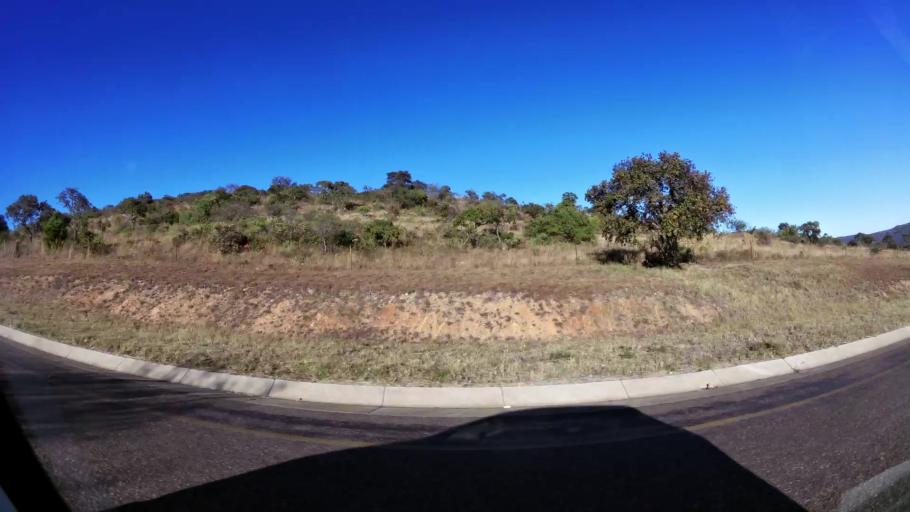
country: ZA
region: Limpopo
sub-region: Capricorn District Municipality
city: Mankoeng
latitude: -23.9239
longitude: 29.8926
